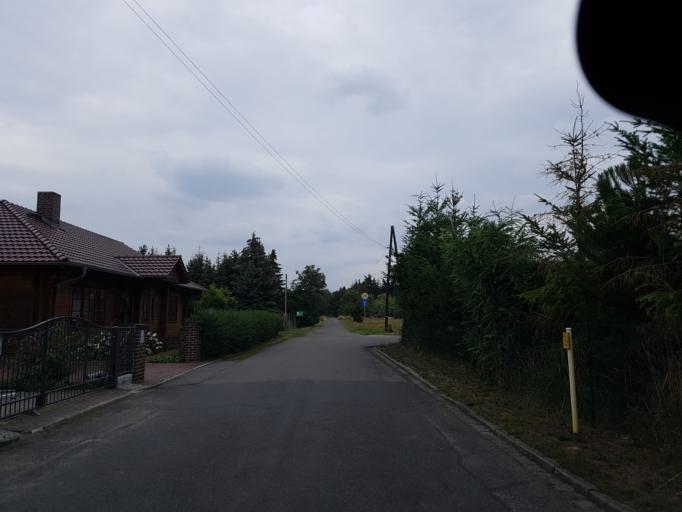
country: DE
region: Brandenburg
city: Schipkau
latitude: 51.5542
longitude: 13.8856
